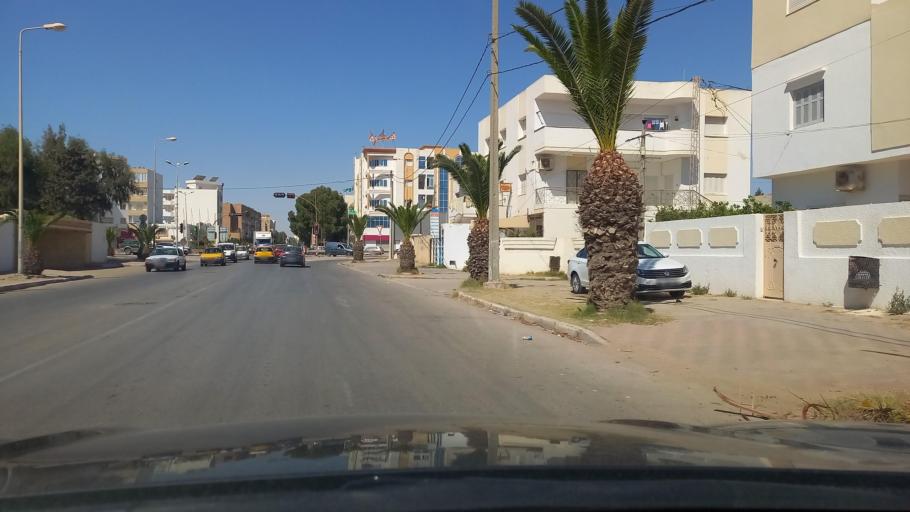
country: TN
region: Safaqis
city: Sfax
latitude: 34.7275
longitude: 10.7271
